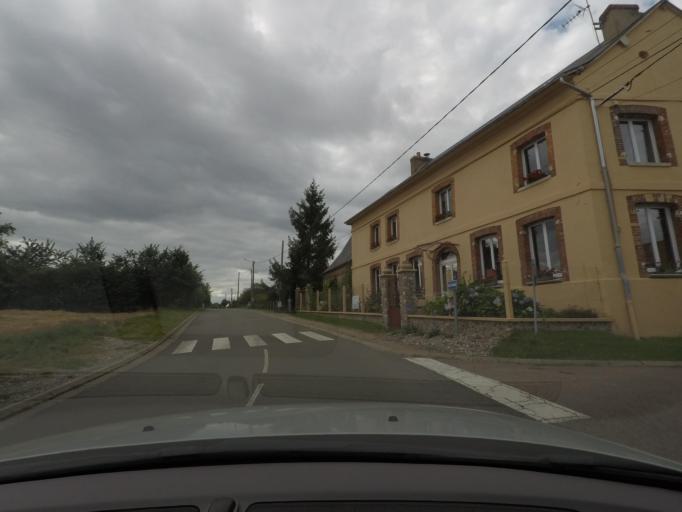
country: FR
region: Haute-Normandie
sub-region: Departement de l'Eure
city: Fleury-sur-Andelle
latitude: 49.2852
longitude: 1.3452
